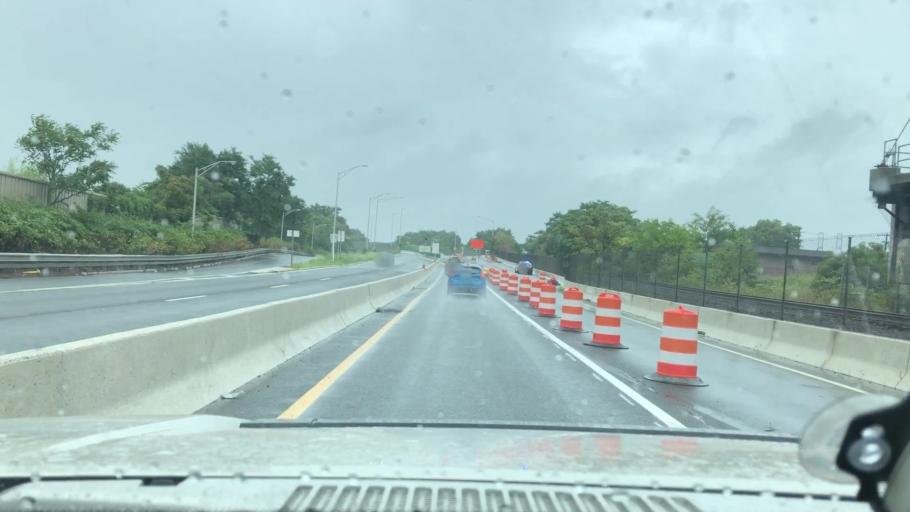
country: US
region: New Jersey
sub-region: Hudson County
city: Bayonne
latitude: 40.6542
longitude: -74.1303
